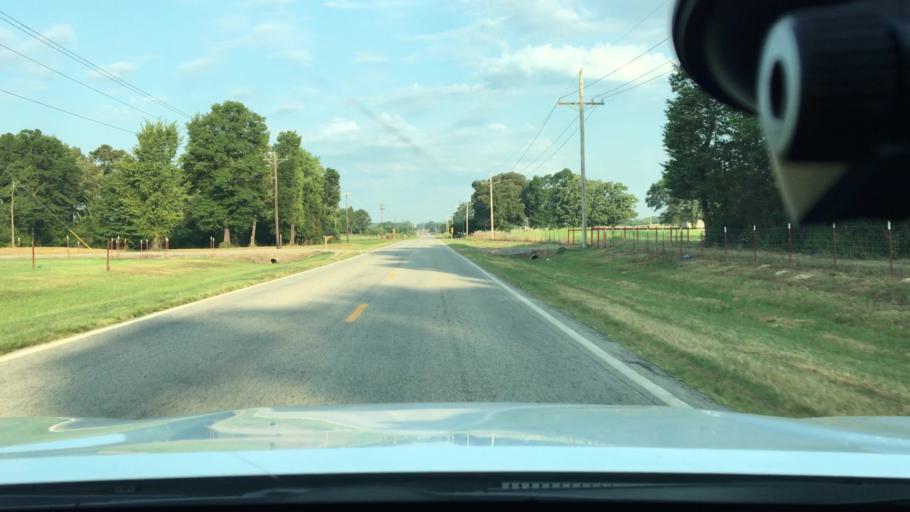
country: US
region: Arkansas
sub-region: Johnson County
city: Coal Hill
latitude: 35.3372
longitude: -93.6159
